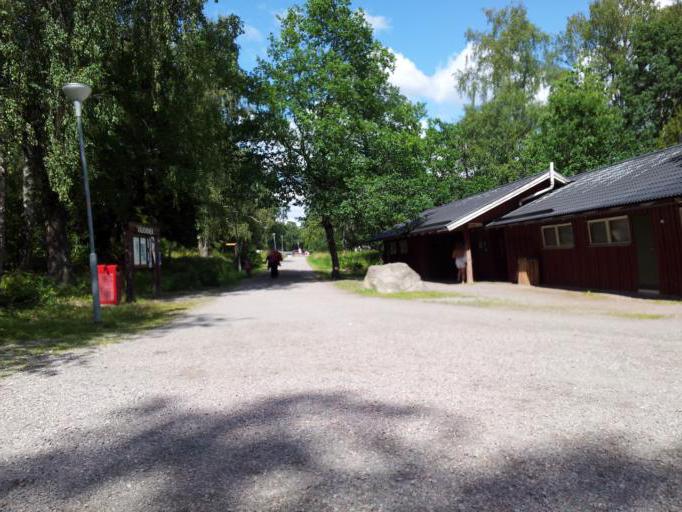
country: SE
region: Uppsala
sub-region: Knivsta Kommun
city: Knivsta
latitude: 59.8331
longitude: 17.9120
